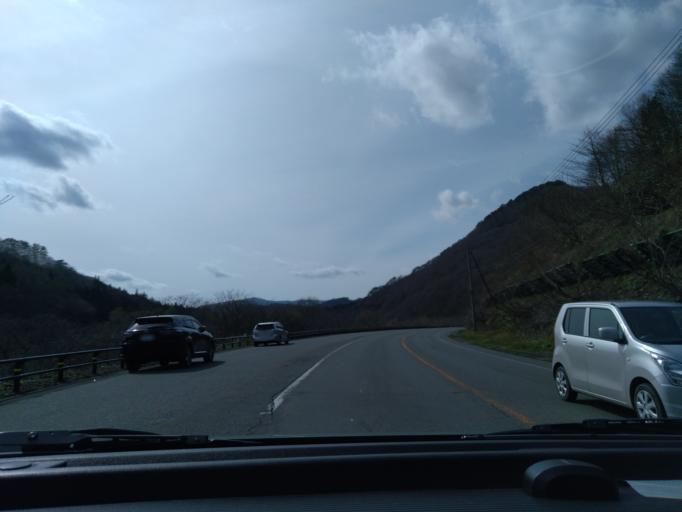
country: JP
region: Akita
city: Yokotemachi
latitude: 39.3129
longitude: 140.8029
